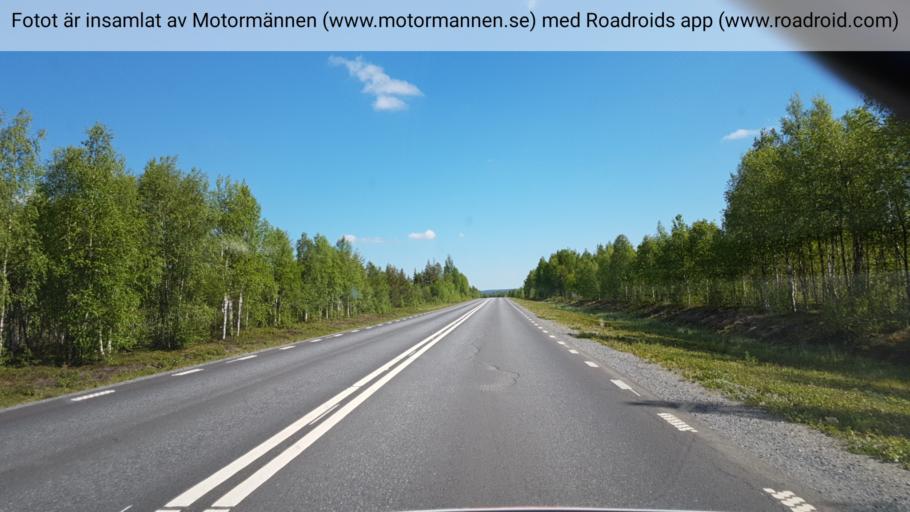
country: SE
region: Vaesterbotten
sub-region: Dorotea Kommun
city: Dorotea
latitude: 64.3209
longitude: 16.6147
